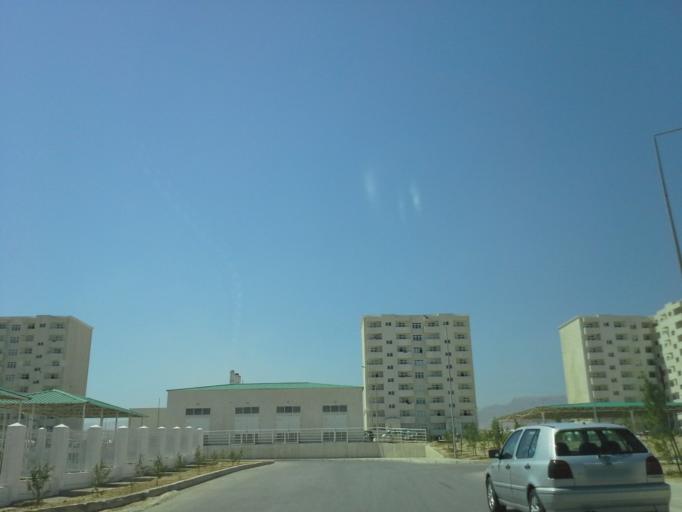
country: TM
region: Ahal
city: Ashgabat
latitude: 37.8874
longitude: 58.4073
